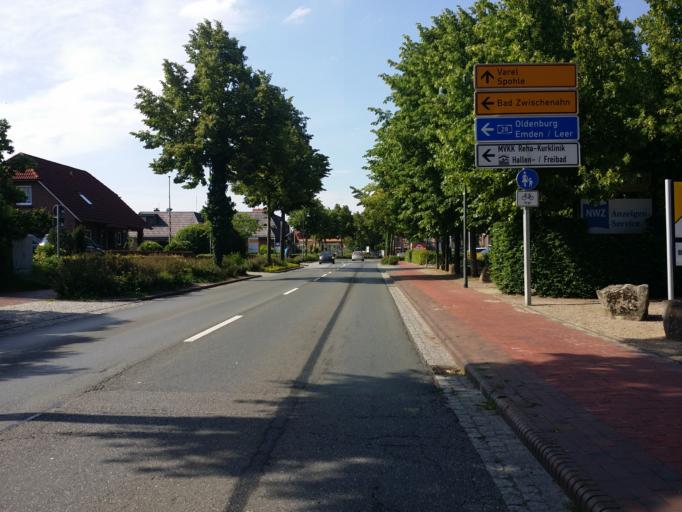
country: DE
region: Lower Saxony
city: Wiefelstede
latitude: 53.2538
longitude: 8.1170
